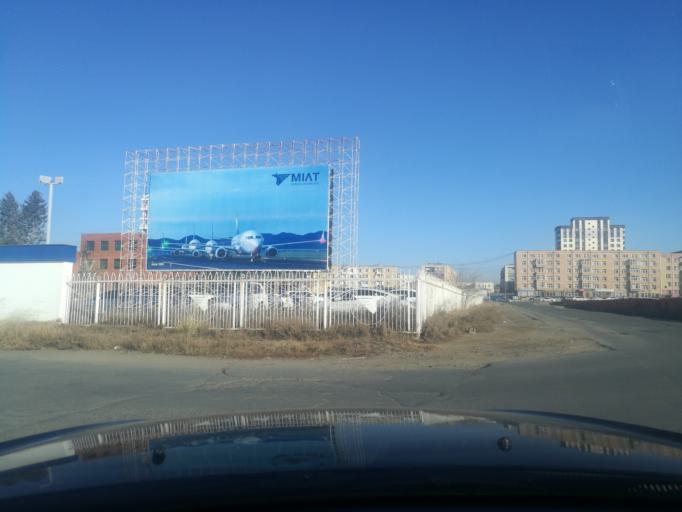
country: MN
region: Ulaanbaatar
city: Ulaanbaatar
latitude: 47.8542
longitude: 106.7607
